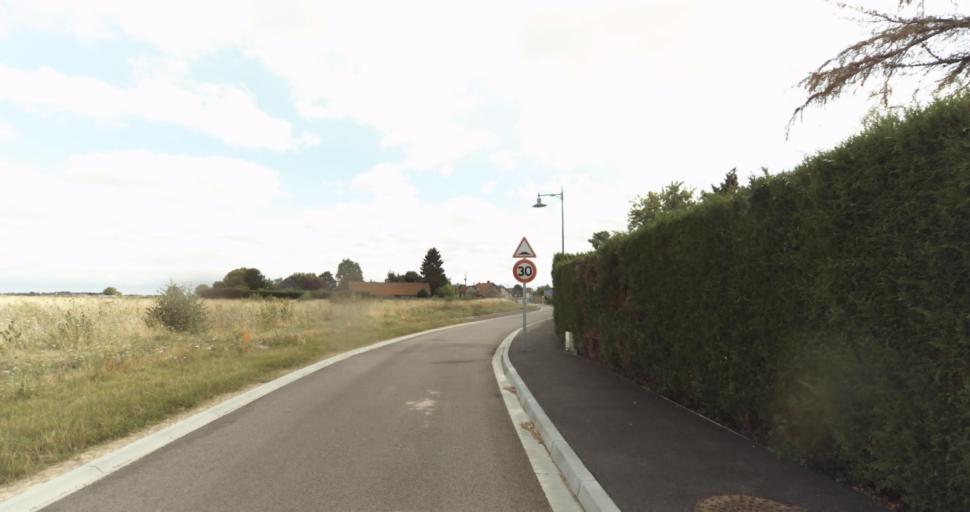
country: FR
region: Haute-Normandie
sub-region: Departement de l'Eure
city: Nonancourt
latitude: 48.8417
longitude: 1.1647
